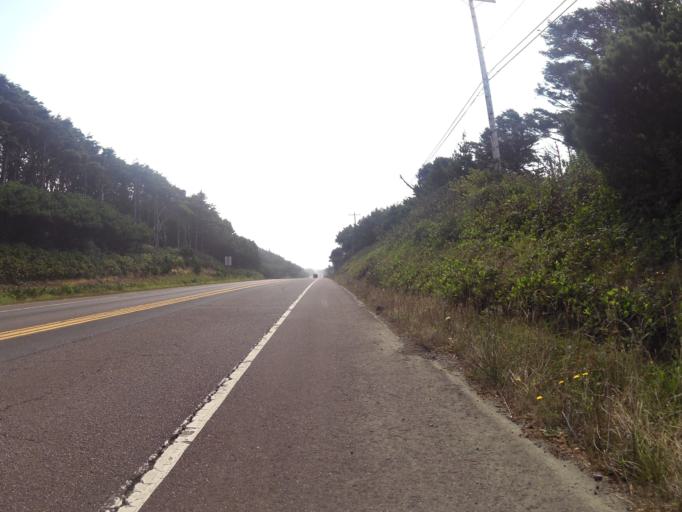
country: US
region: Oregon
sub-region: Lincoln County
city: Newport
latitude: 44.5508
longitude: -124.0725
